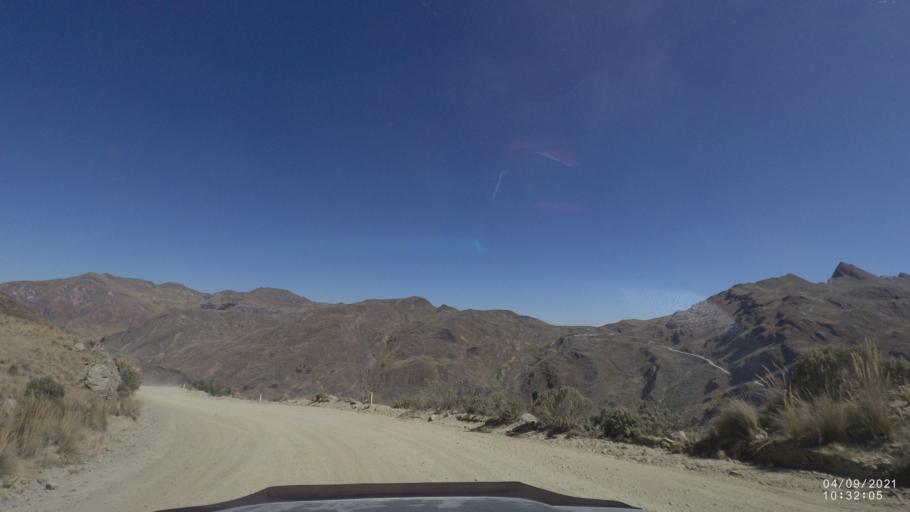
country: BO
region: Cochabamba
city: Sipe Sipe
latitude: -17.2985
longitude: -66.4463
